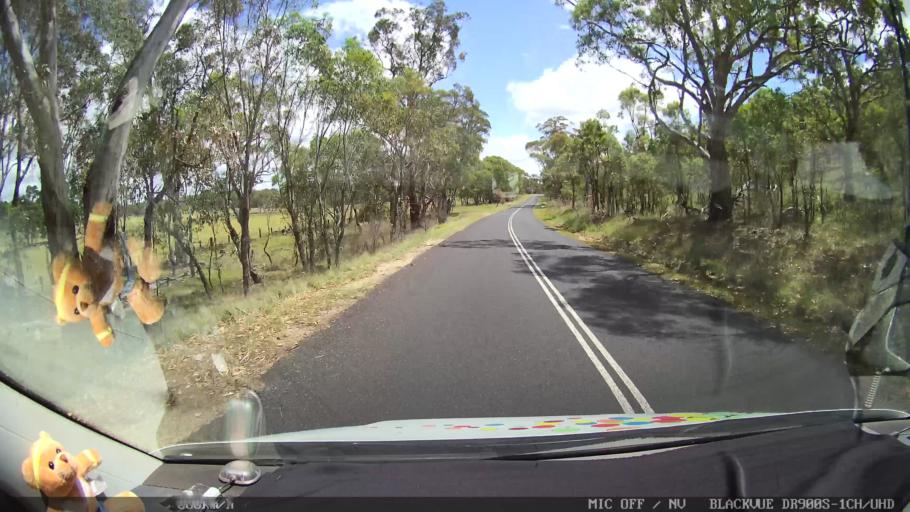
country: AU
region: New South Wales
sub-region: Glen Innes Severn
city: Glen Innes
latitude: -29.5302
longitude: 151.6735
